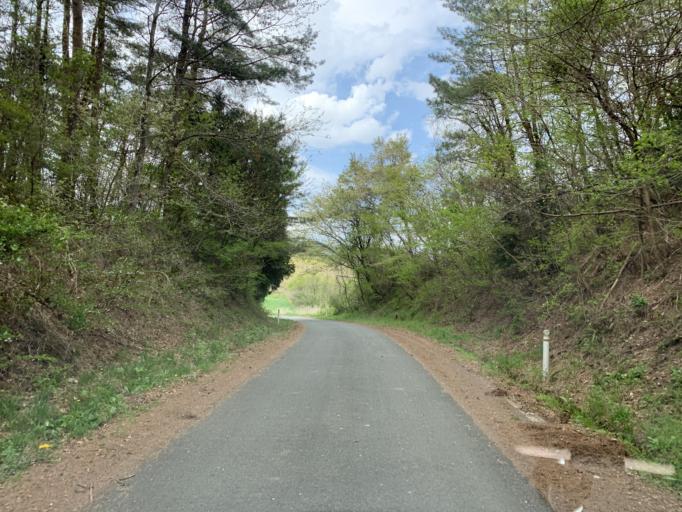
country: JP
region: Iwate
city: Ichinoseki
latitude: 38.7878
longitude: 141.4346
